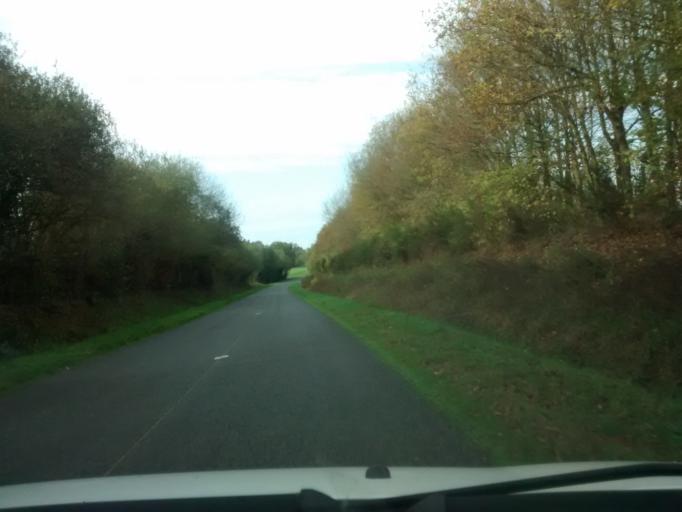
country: FR
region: Brittany
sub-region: Departement d'Ille-et-Vilaine
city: Noyal-sur-Vilaine
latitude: 48.1167
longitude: -1.5034
